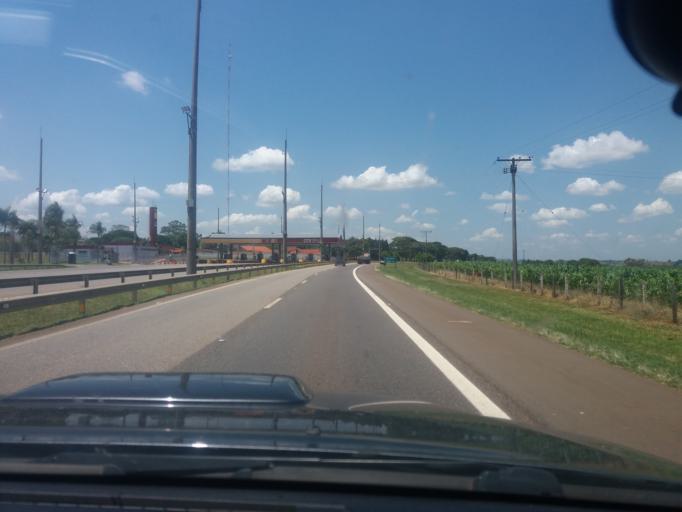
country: BR
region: Sao Paulo
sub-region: Tatui
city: Tatui
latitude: -23.4334
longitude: -47.9375
